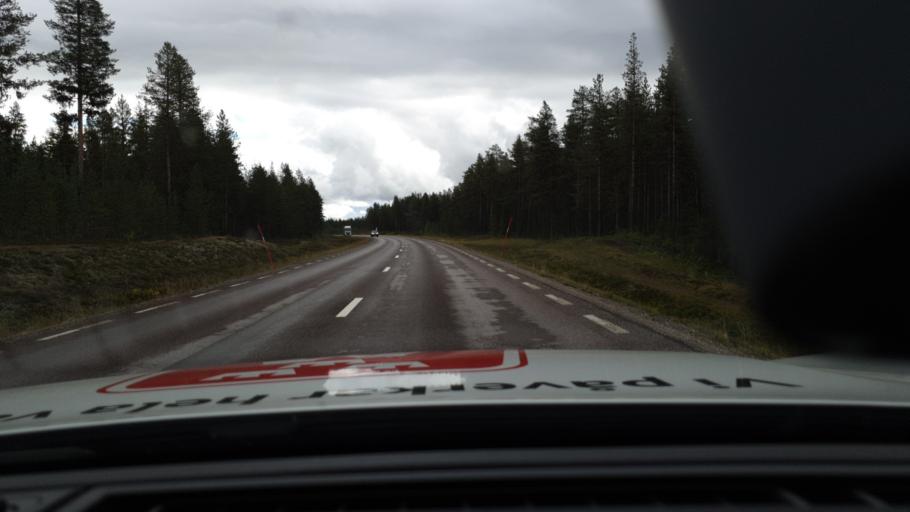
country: SE
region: Norrbotten
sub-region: Gallivare Kommun
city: Gaellivare
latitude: 66.9305
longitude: 21.4836
